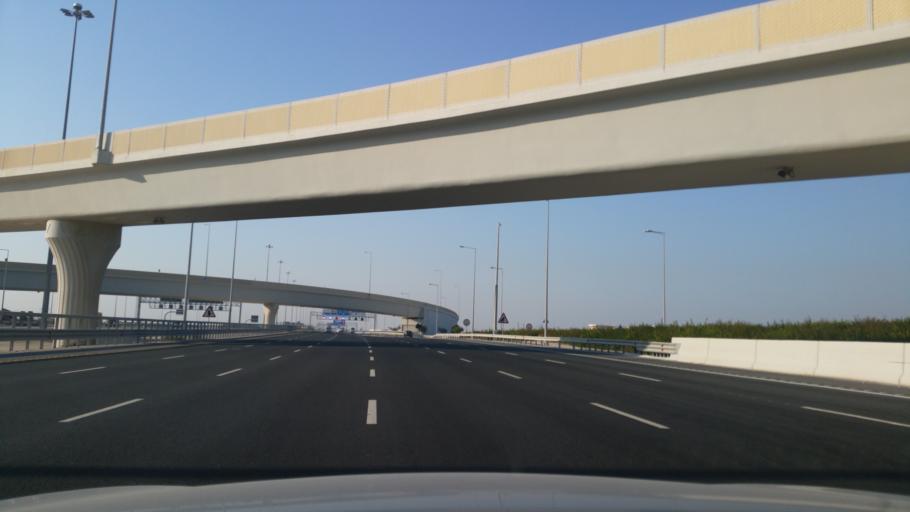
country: QA
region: Al Wakrah
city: Al Wakrah
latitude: 25.1335
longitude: 51.5856
